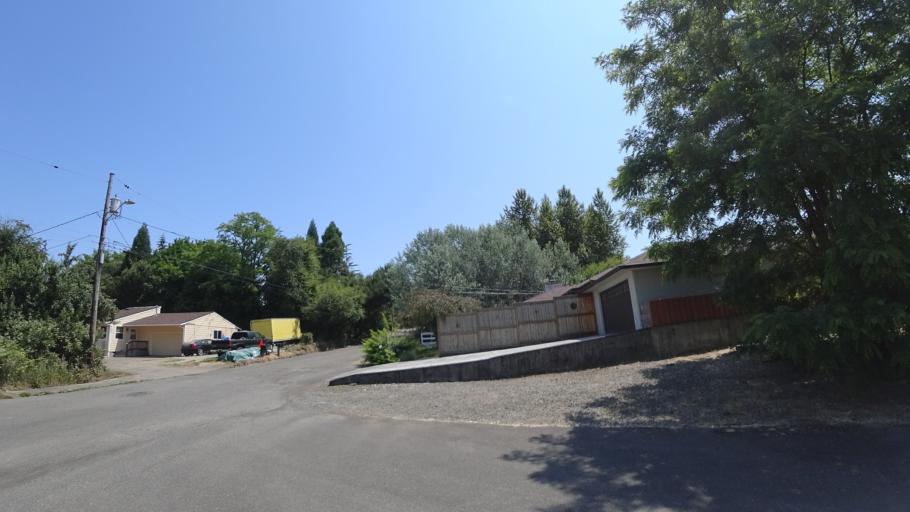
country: US
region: Oregon
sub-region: Multnomah County
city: Lents
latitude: 45.4574
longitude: -122.5716
